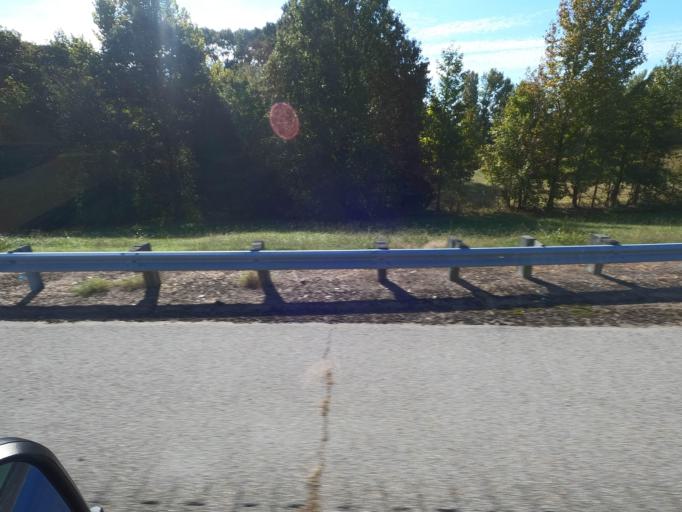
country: US
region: Tennessee
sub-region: Shelby County
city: Lakeland
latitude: 35.3097
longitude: -89.7794
